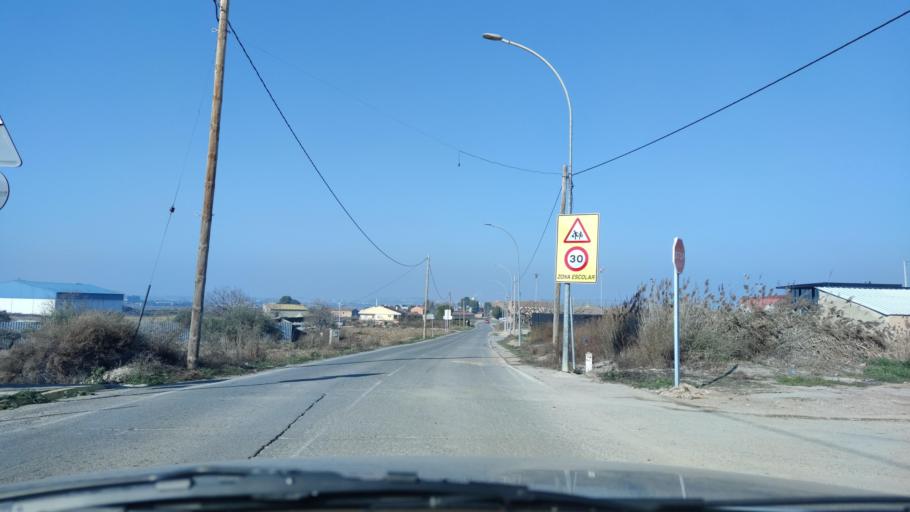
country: ES
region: Catalonia
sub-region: Provincia de Lleida
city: Alcoletge
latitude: 41.6163
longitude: 0.7366
